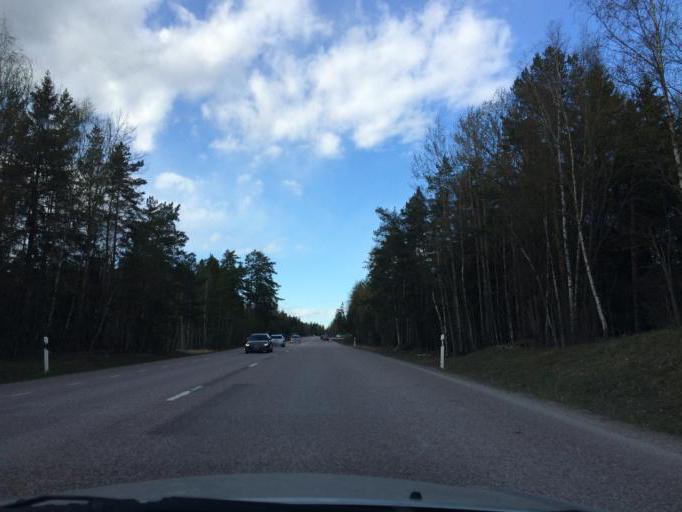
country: SE
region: Vaestmanland
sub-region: Hallstahammars Kommun
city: Kolback
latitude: 59.5763
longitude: 16.3527
